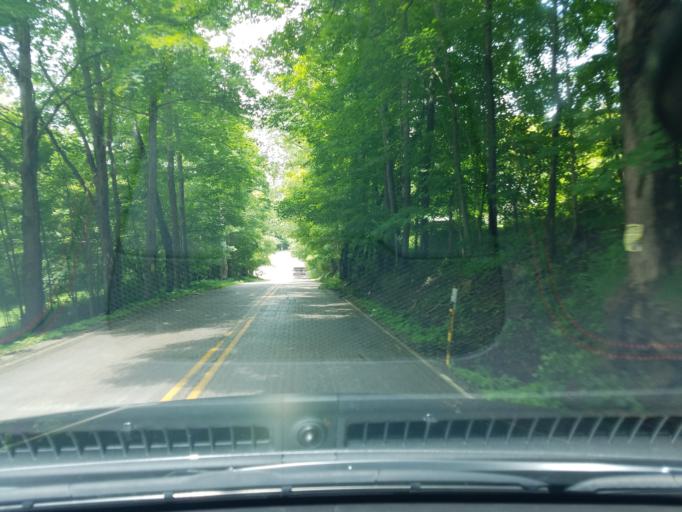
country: US
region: Pennsylvania
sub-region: Fayette County
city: Bear Rocks
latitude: 40.1639
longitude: -79.3554
